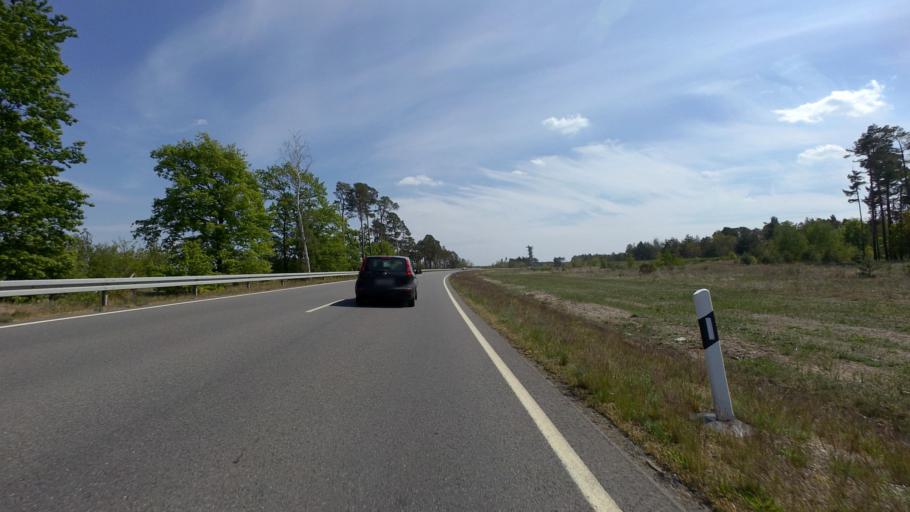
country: DE
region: Brandenburg
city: Cottbus
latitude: 51.7826
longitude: 14.3872
